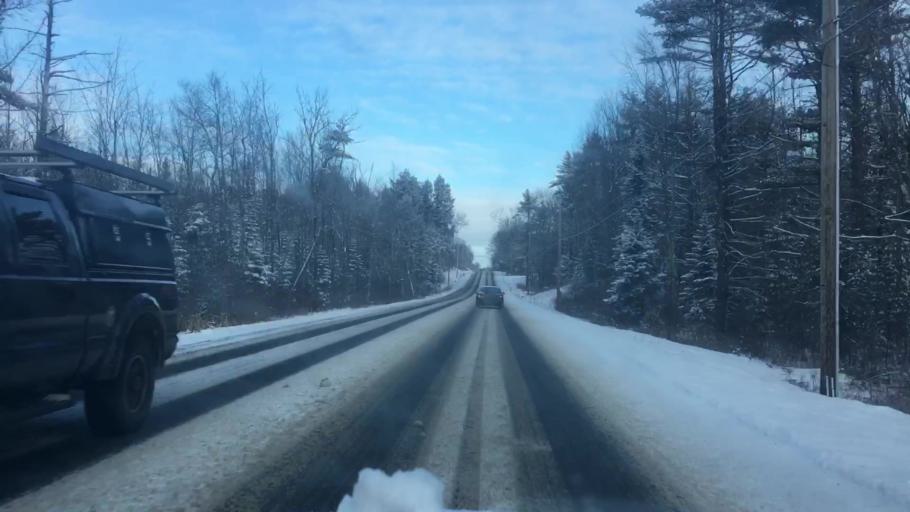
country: US
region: Maine
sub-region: Cumberland County
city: North Windham
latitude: 43.8034
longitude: -70.4404
